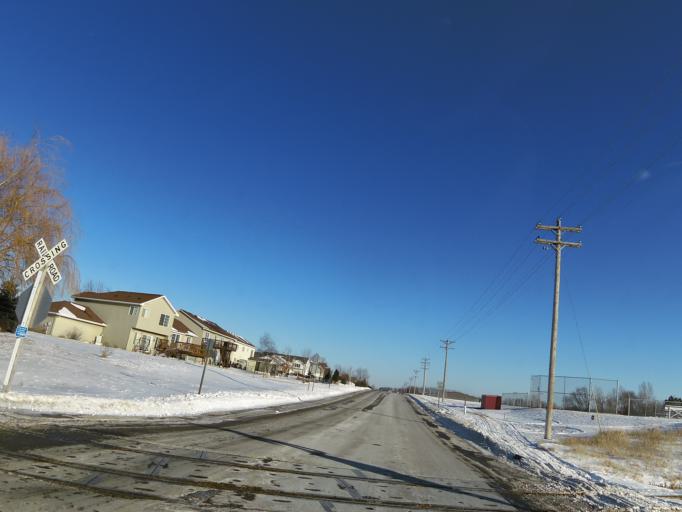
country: US
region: Minnesota
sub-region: Le Sueur County
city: New Prague
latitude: 44.5580
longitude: -93.5834
